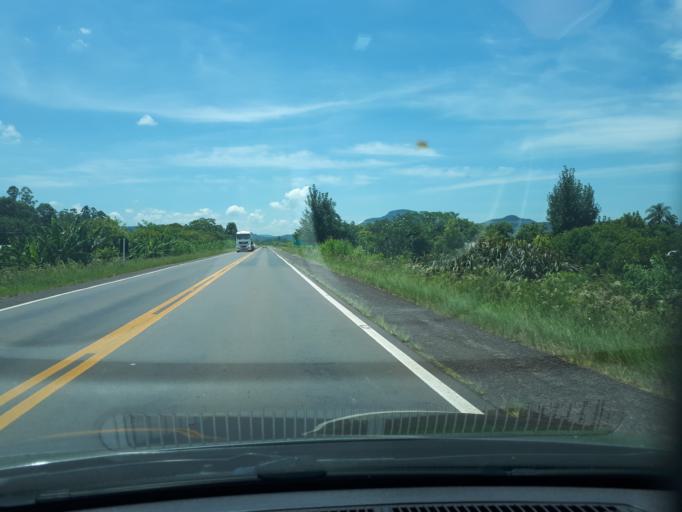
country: BR
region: Rio Grande do Sul
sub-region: Candelaria
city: Candelaria
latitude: -29.7233
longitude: -52.9191
